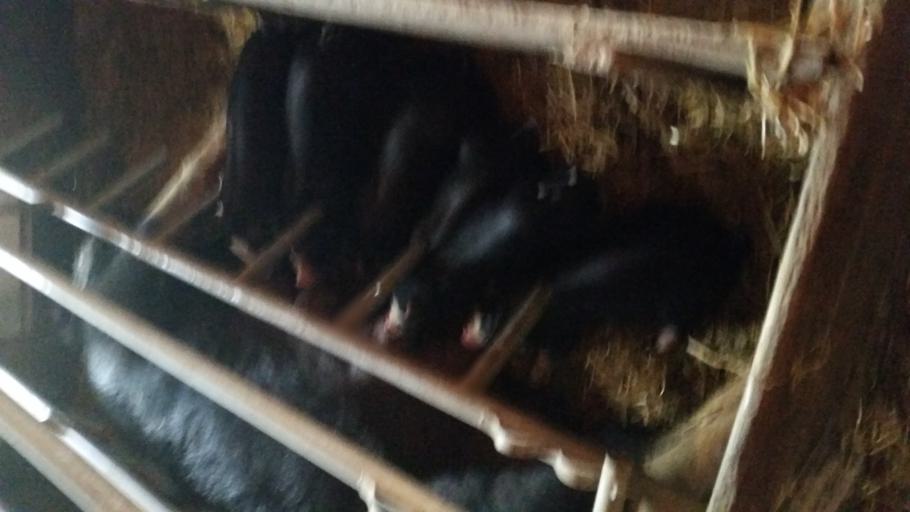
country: US
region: Wisconsin
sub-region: Marathon County
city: Spencer
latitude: 44.6556
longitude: -90.3707
